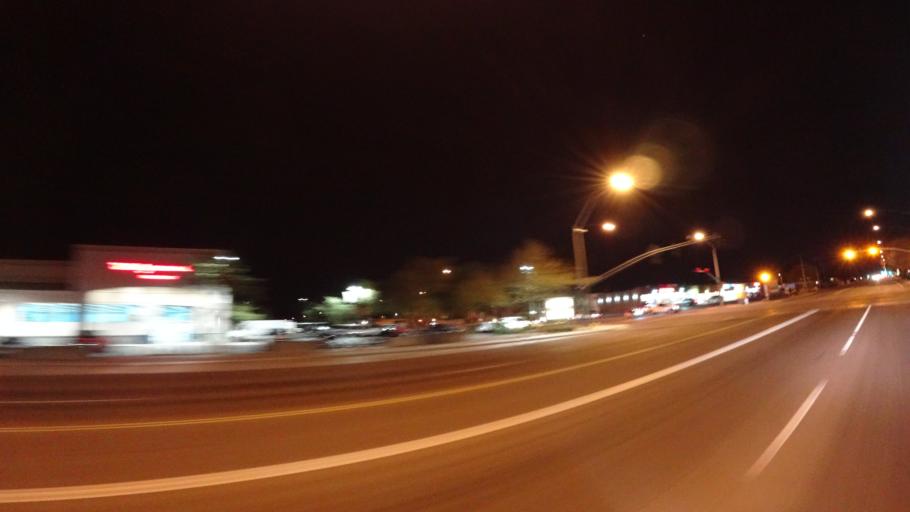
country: US
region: Arizona
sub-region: Maricopa County
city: Mesa
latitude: 33.4361
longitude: -111.8227
